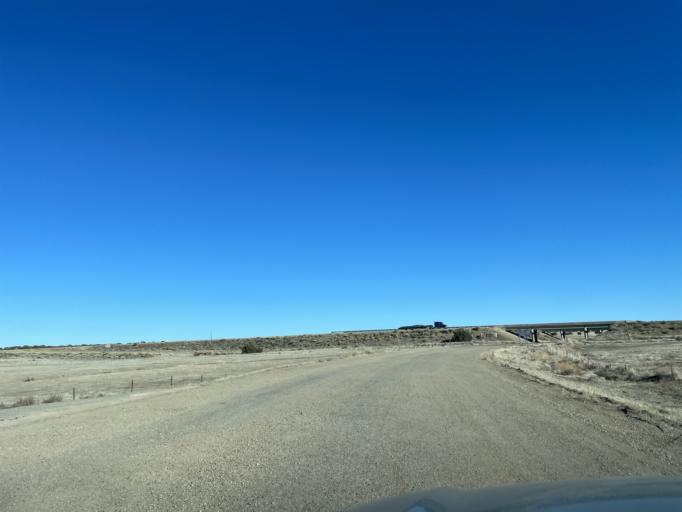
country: US
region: Colorado
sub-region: Mesa County
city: Loma
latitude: 39.1755
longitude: -109.1302
